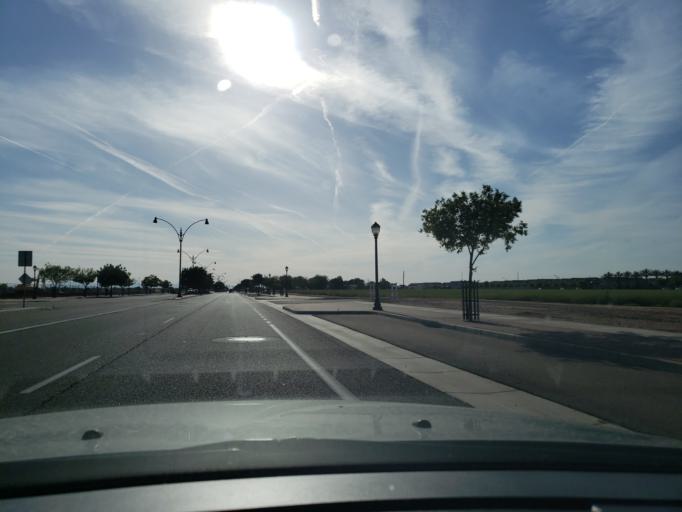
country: US
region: Arizona
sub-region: Maricopa County
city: Queen Creek
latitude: 33.3072
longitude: -111.6970
